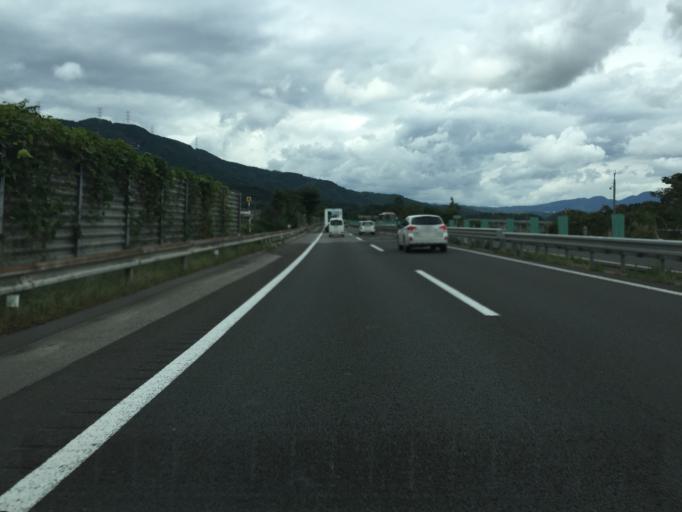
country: JP
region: Miyagi
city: Shiroishi
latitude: 37.9650
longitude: 140.6181
